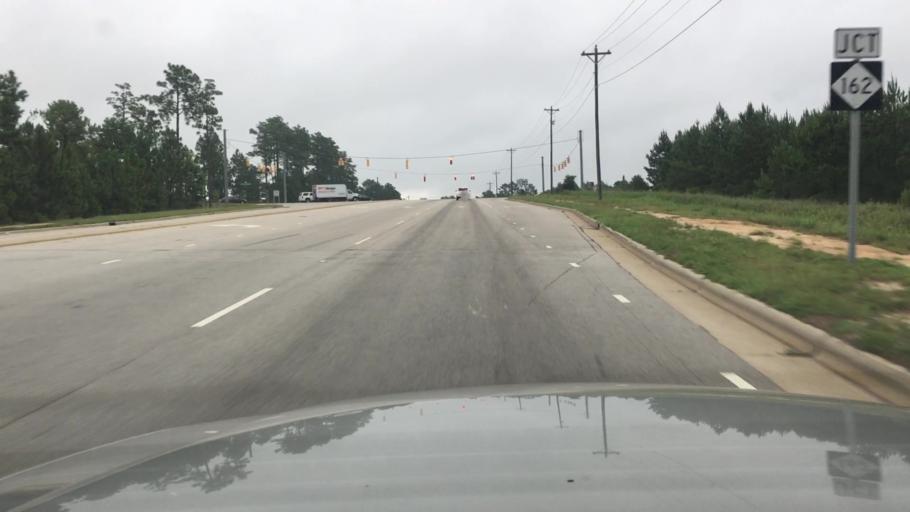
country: US
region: North Carolina
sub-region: Cumberland County
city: Hope Mills
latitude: 34.9902
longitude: -78.9503
